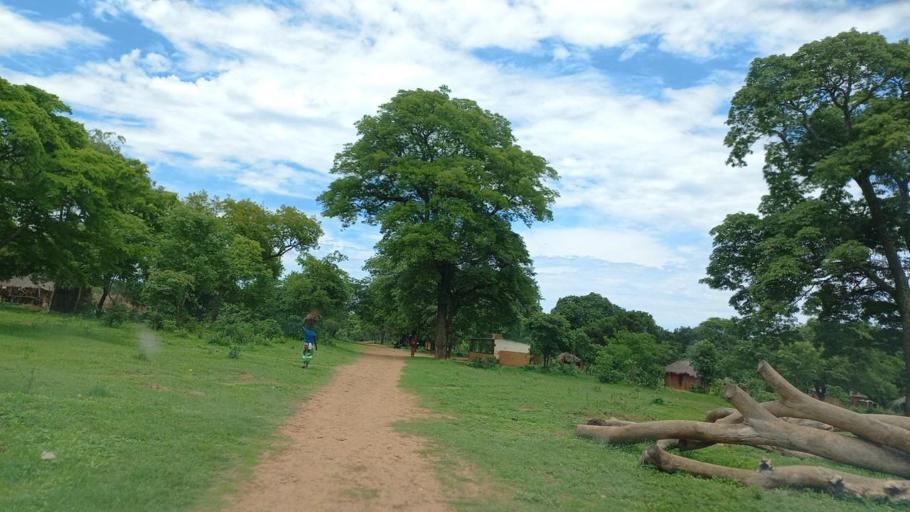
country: ZM
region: North-Western
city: Kabompo
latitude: -13.6097
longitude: 24.2471
